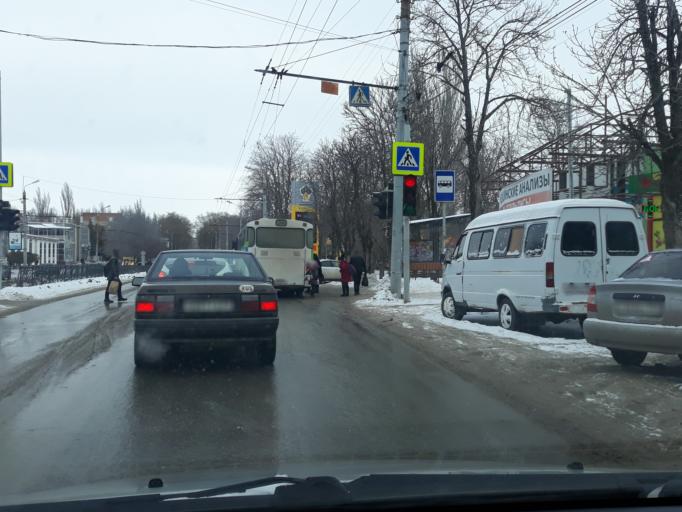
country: RU
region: Rostov
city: Taganrog
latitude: 47.2517
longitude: 38.9179
